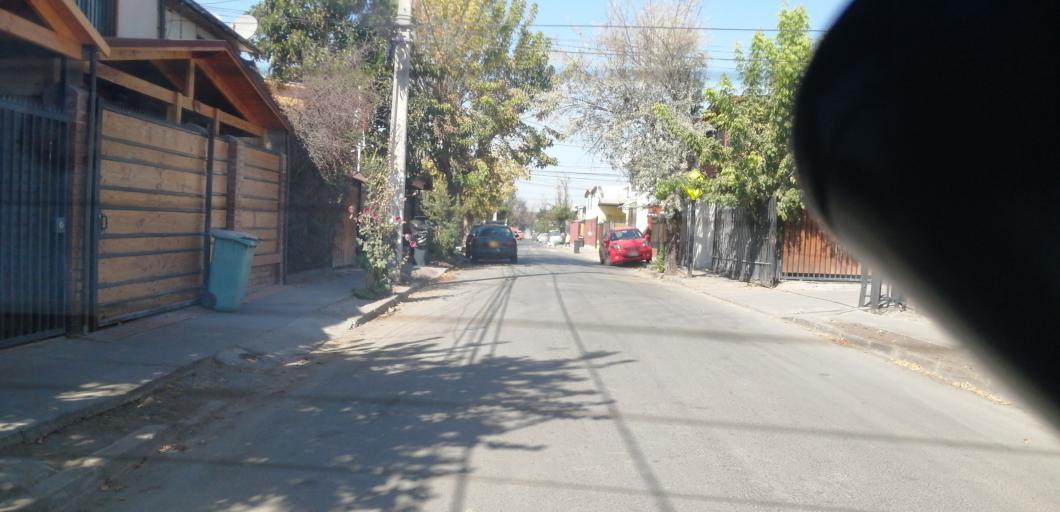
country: CL
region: Santiago Metropolitan
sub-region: Provincia de Santiago
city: Lo Prado
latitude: -33.4644
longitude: -70.7456
